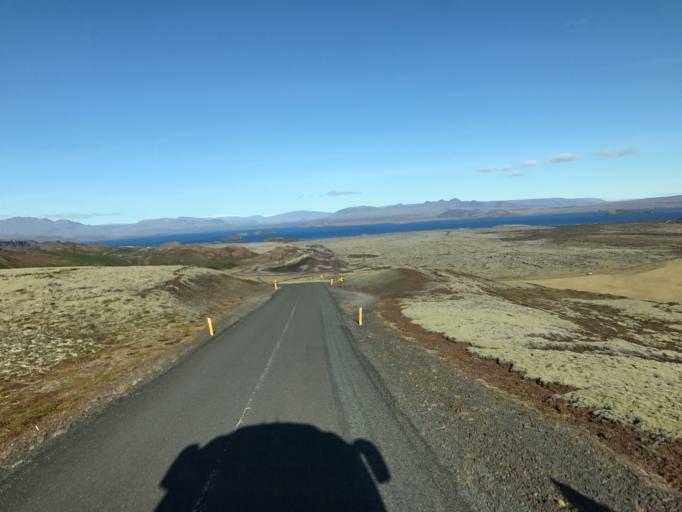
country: IS
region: South
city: Hveragerdi
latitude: 64.1156
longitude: -21.2646
